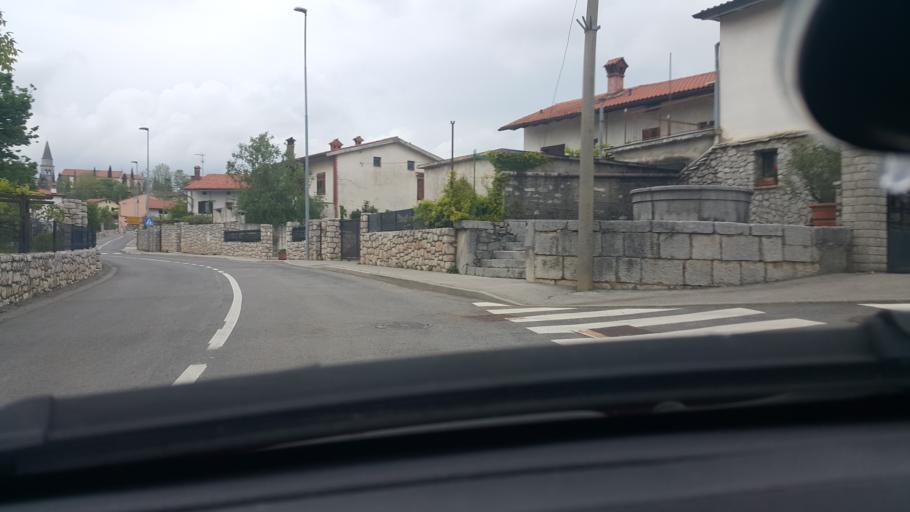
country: SI
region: Komen
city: Komen
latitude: 45.8150
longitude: 13.7490
